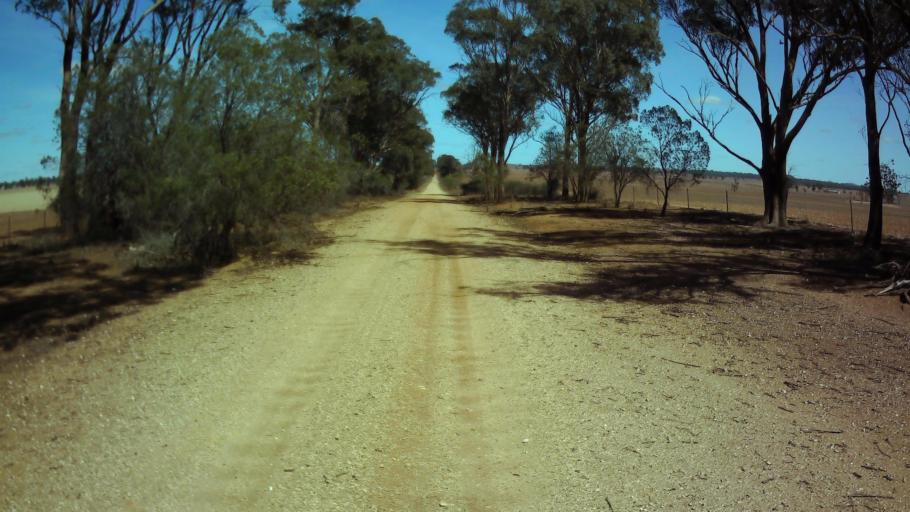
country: AU
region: New South Wales
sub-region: Weddin
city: Grenfell
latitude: -33.7267
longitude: 147.8796
